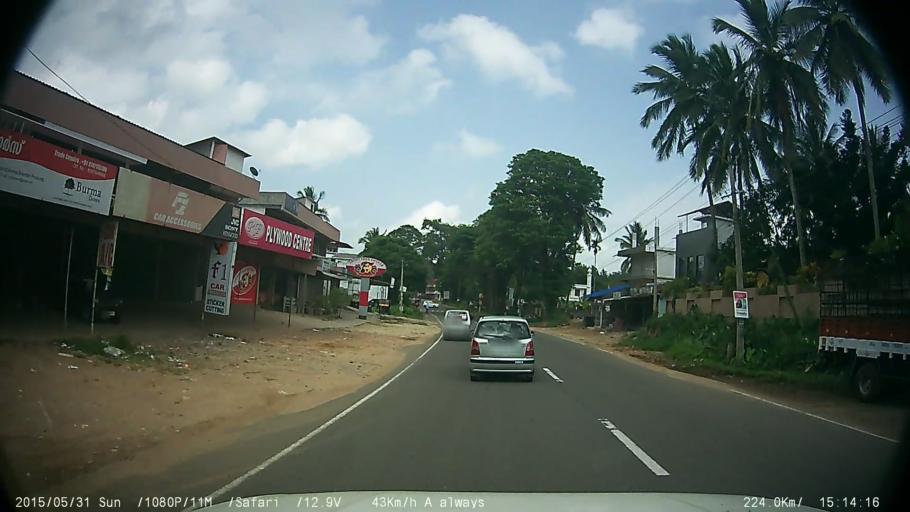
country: IN
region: Kerala
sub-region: Wayanad
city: Panamaram
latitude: 11.6596
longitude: 76.2444
